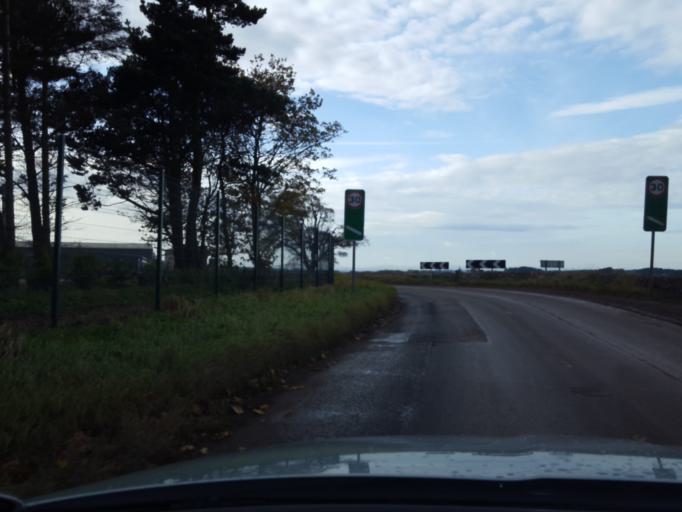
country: GB
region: Scotland
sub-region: South Lanarkshire
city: Carnwath
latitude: 55.7053
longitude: -3.6157
